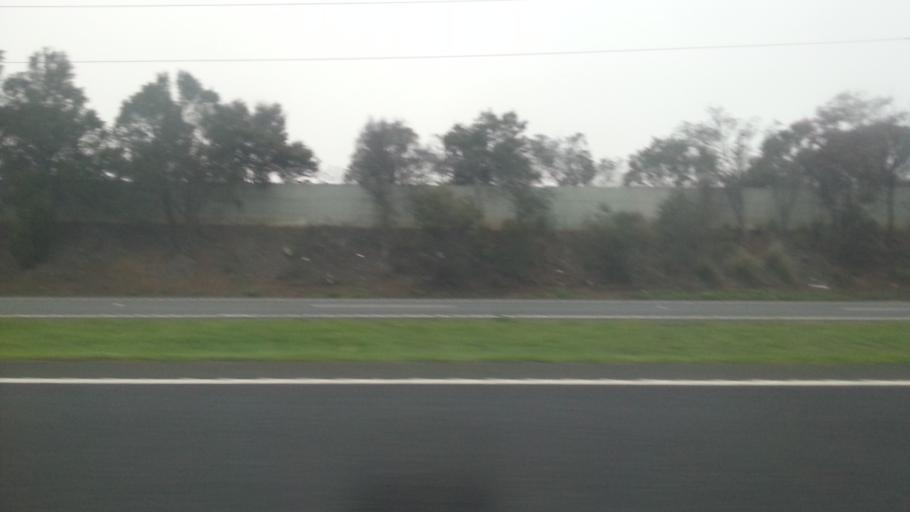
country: AU
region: New South Wales
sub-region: Camden
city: Narellan Vale
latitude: -34.0489
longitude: 150.7424
